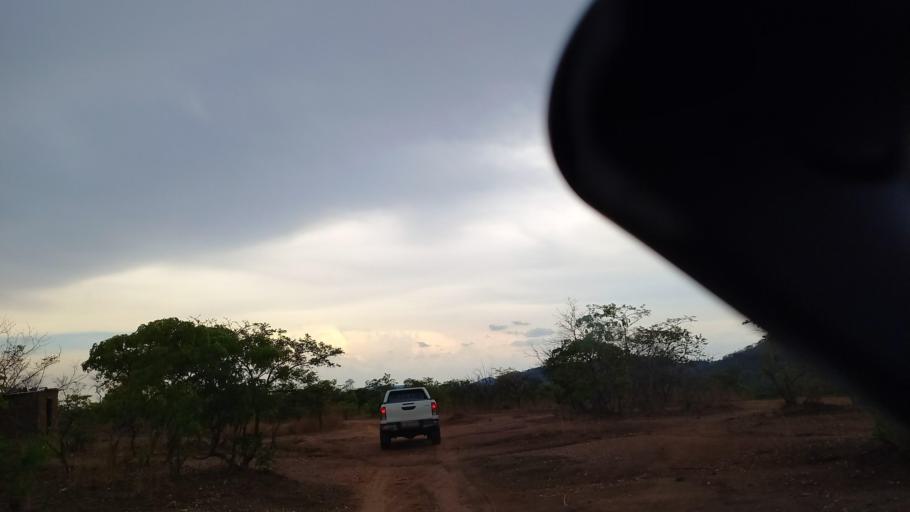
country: ZM
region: Lusaka
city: Kafue
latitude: -16.0314
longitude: 28.3034
